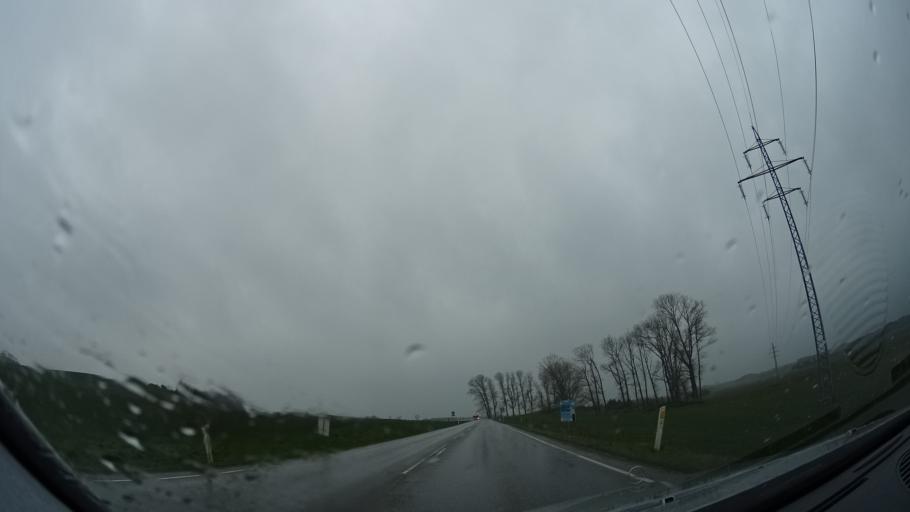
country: DK
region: Zealand
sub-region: Holbaek Kommune
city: Holbaek
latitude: 55.7581
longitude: 11.6272
